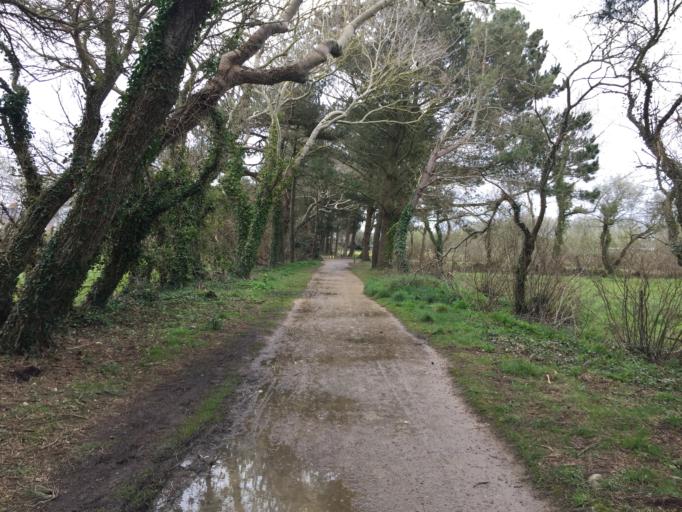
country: JE
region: St Helier
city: Saint Helier
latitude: 49.1822
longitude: -2.2261
